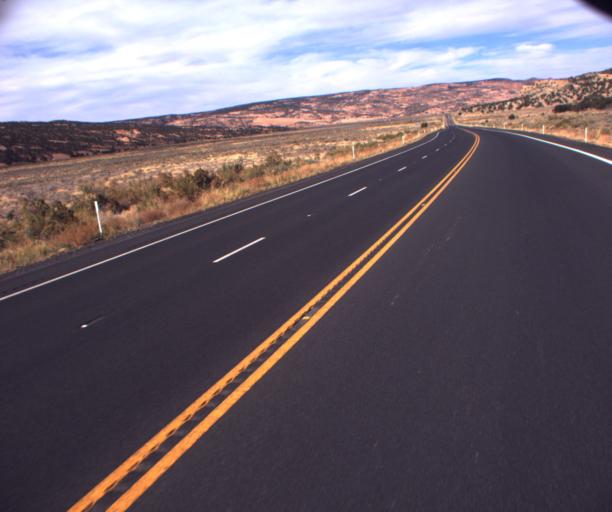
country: US
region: Arizona
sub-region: Navajo County
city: Kayenta
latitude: 36.5832
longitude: -110.4717
